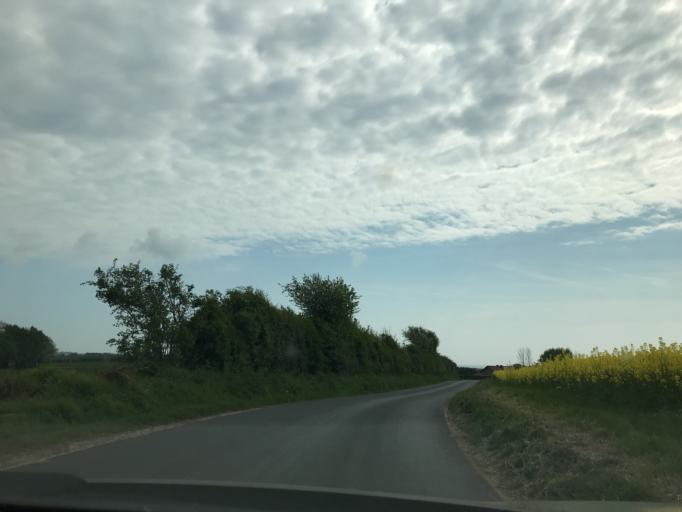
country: DK
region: South Denmark
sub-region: Assens Kommune
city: Assens
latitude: 55.3321
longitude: 9.8977
